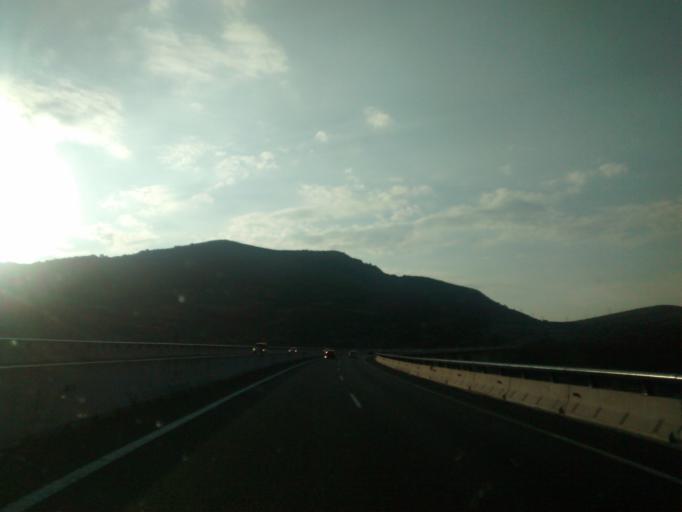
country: ES
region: Cantabria
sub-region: Provincia de Cantabria
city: Arenas de Iguna
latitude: 43.1891
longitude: -4.0660
